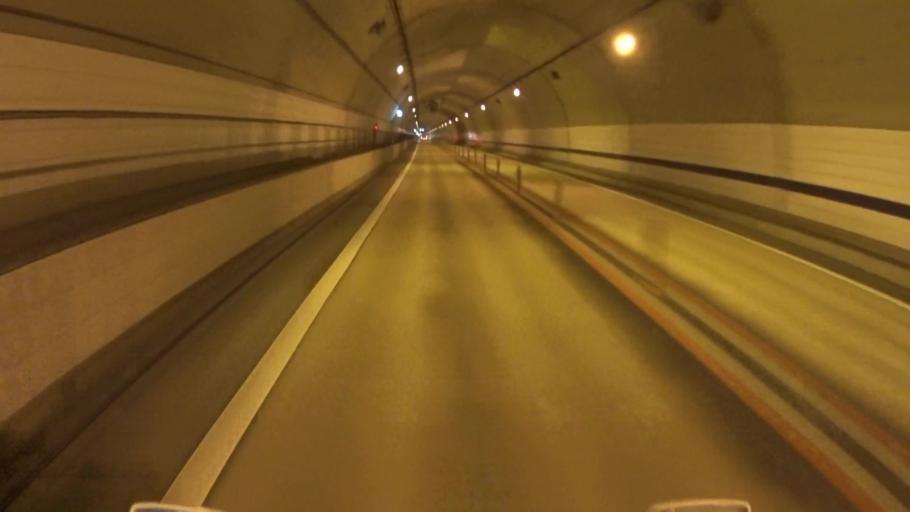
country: JP
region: Kyoto
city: Miyazu
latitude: 35.4895
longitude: 135.1720
